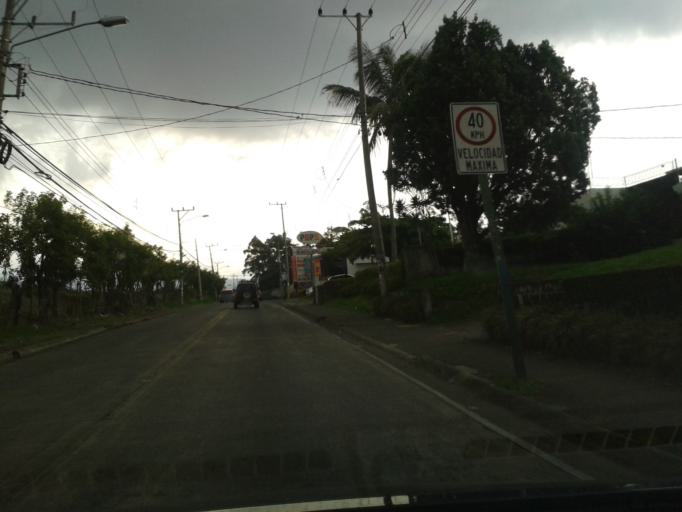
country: CR
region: Heredia
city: San Francisco
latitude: 9.9933
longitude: -84.1308
